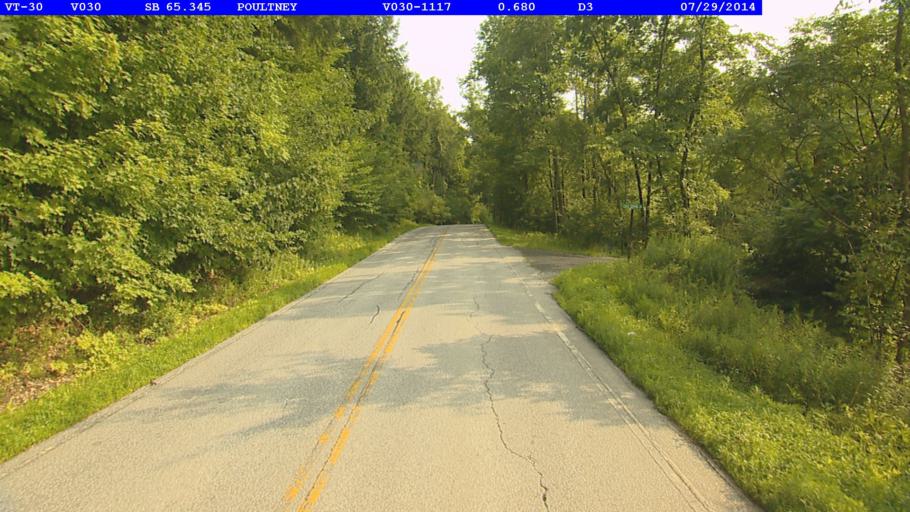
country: US
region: Vermont
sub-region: Rutland County
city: Poultney
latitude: 43.4735
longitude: -73.2023
